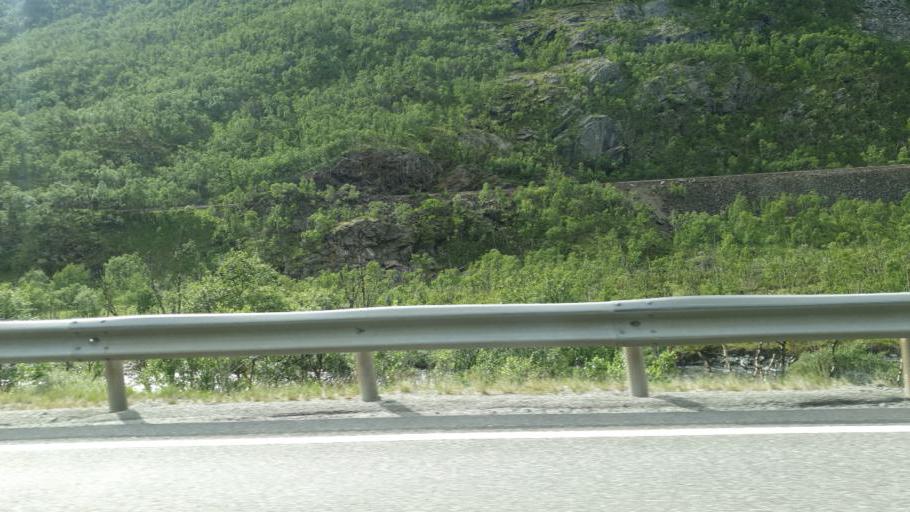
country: NO
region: Sor-Trondelag
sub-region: Oppdal
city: Oppdal
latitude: 62.3261
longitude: 9.6220
